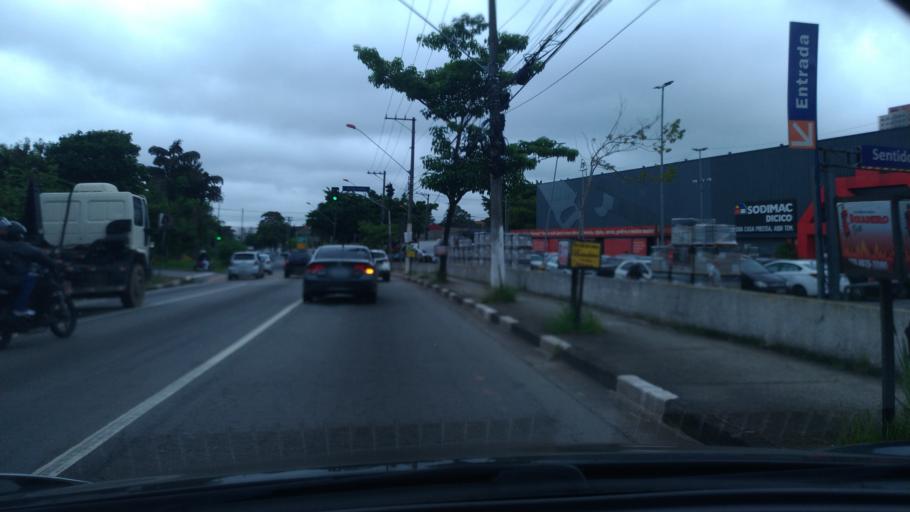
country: BR
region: Sao Paulo
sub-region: Diadema
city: Diadema
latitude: -23.6808
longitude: -46.5972
